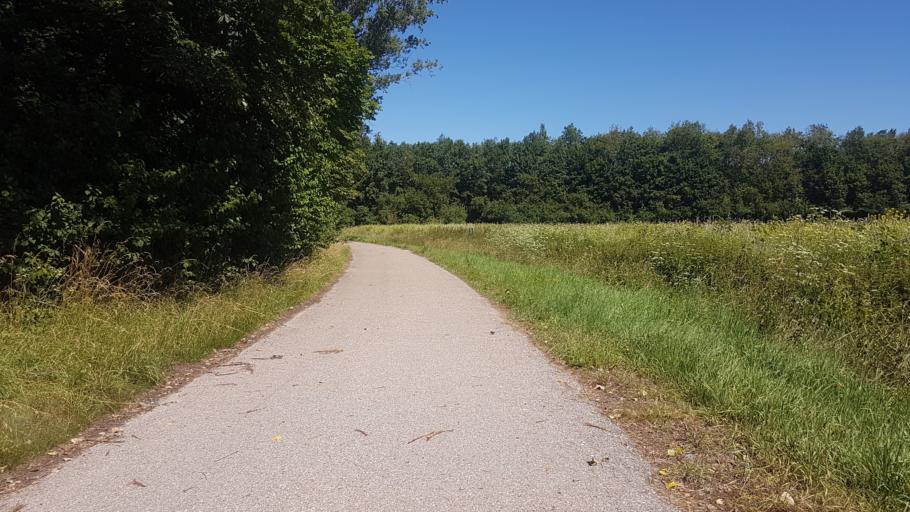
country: DE
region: Bavaria
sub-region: Regierungsbezirk Mittelfranken
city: Herrieden
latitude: 49.2478
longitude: 10.4670
